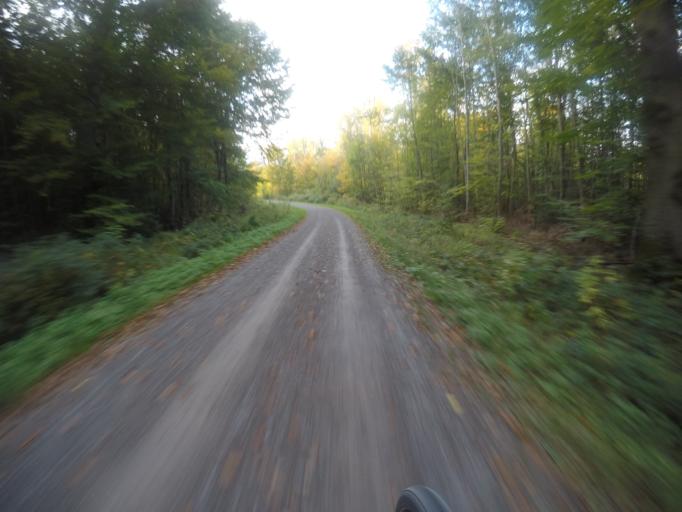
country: DE
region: Baden-Wuerttemberg
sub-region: Regierungsbezirk Stuttgart
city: Weil im Schonbuch
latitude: 48.6118
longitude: 9.0402
